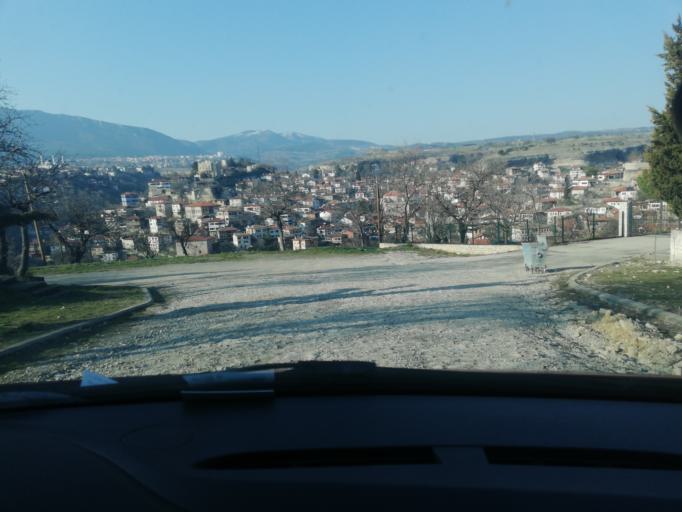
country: TR
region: Karabuk
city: Safranbolu
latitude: 41.2404
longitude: 32.6925
